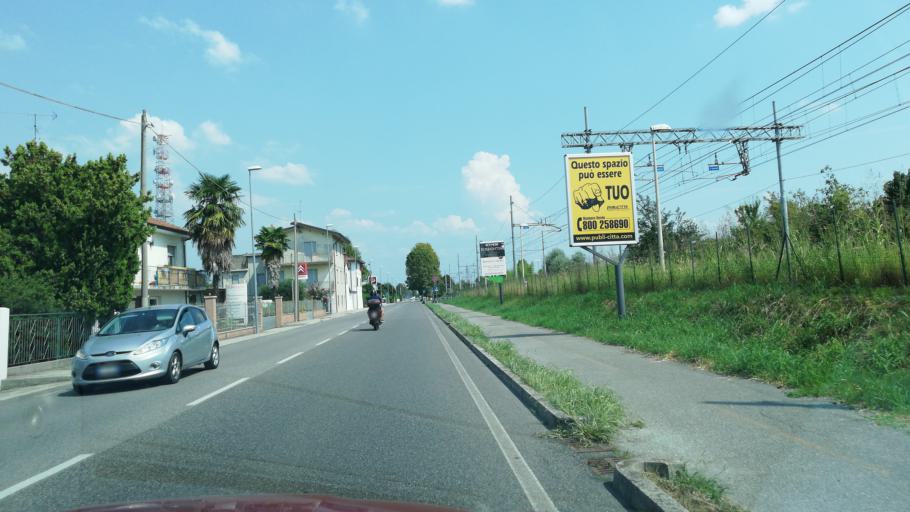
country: IT
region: Friuli Venezia Giulia
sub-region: Provincia di Udine
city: Latisana
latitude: 45.7843
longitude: 13.0059
